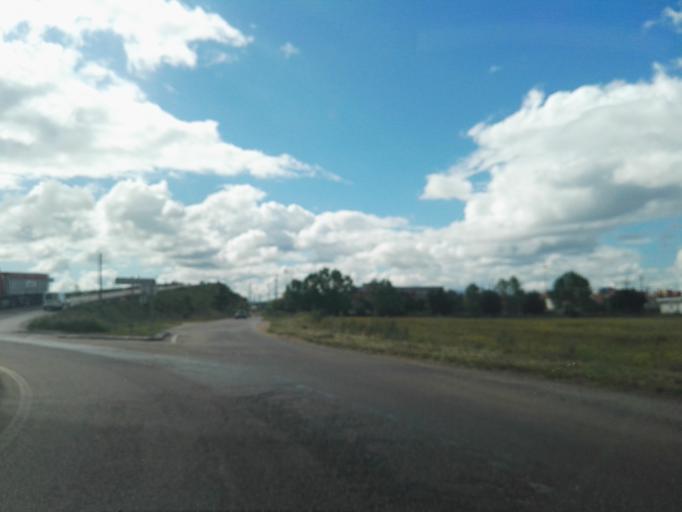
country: PT
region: Santarem
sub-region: Torres Novas
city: Riachos
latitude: 39.4425
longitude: -8.4903
